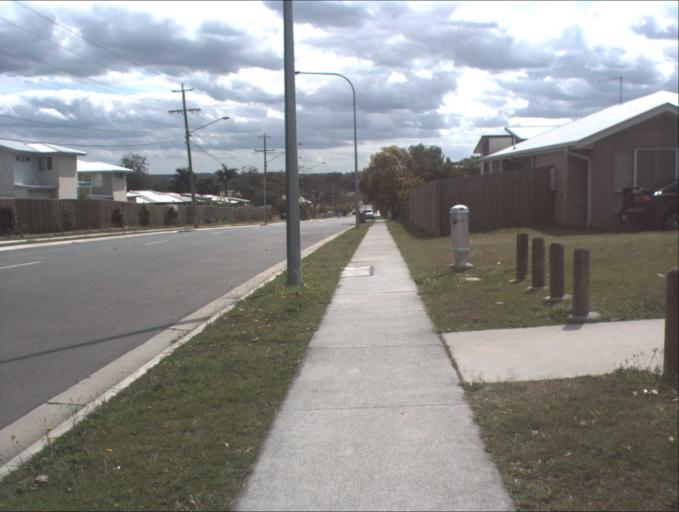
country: AU
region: Queensland
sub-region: Logan
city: Waterford West
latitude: -27.6777
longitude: 153.0938
